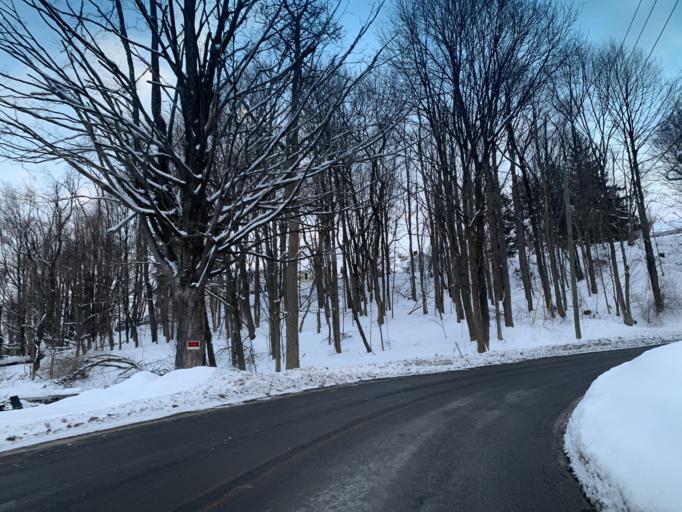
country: US
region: Maryland
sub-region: Allegany County
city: Frostburg
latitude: 39.6590
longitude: -78.9257
